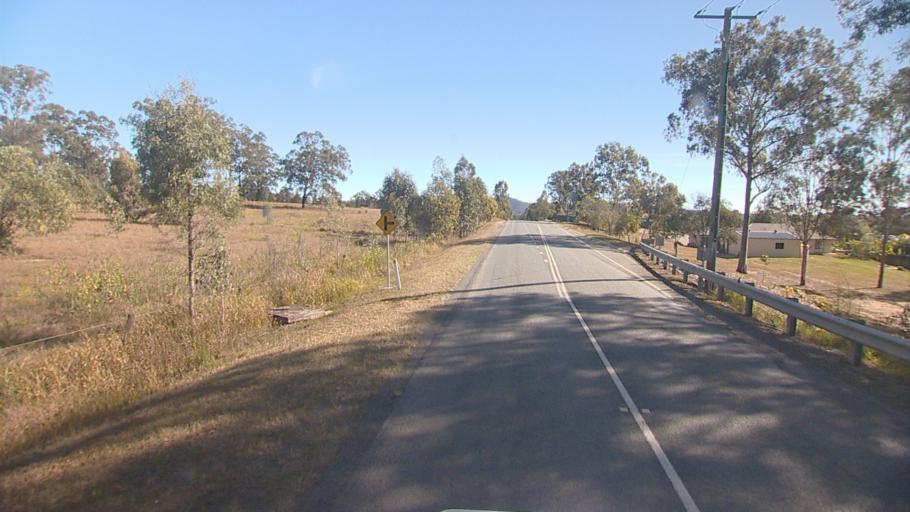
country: AU
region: Queensland
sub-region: Ipswich
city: Springfield Lakes
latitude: -27.7314
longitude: 152.9374
